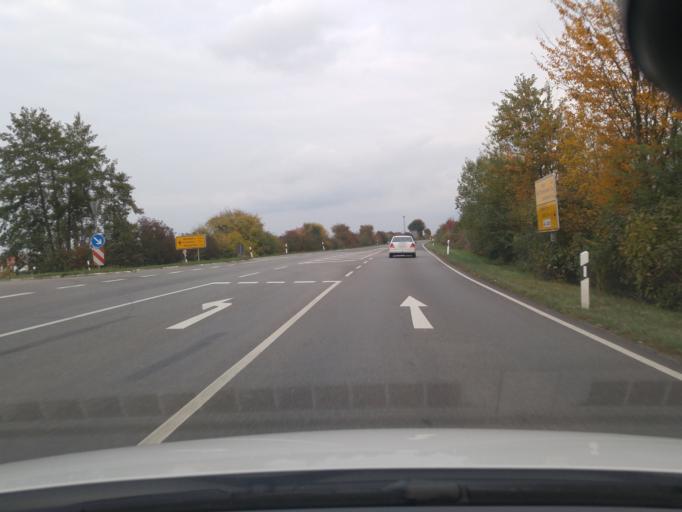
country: DE
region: Rheinland-Pfalz
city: Lustadt
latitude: 49.2533
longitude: 8.2675
